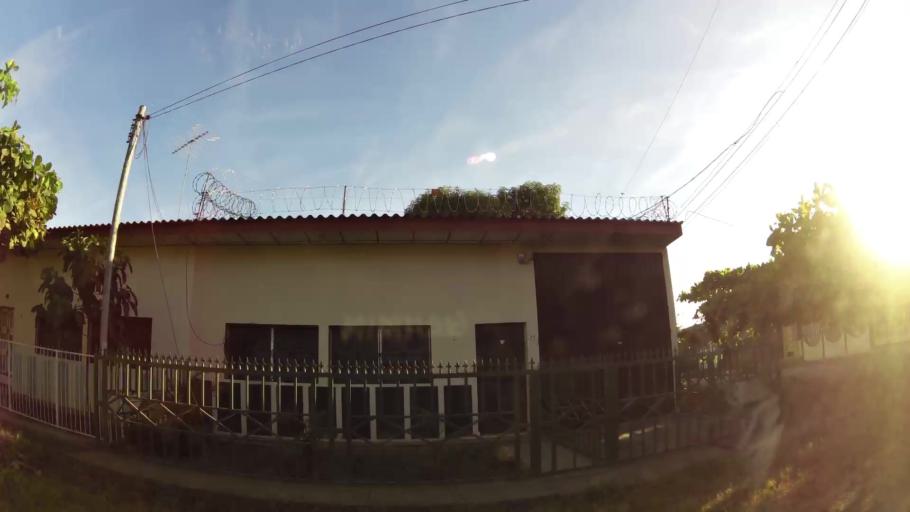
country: SV
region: San Miguel
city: San Miguel
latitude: 13.4628
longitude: -88.1708
